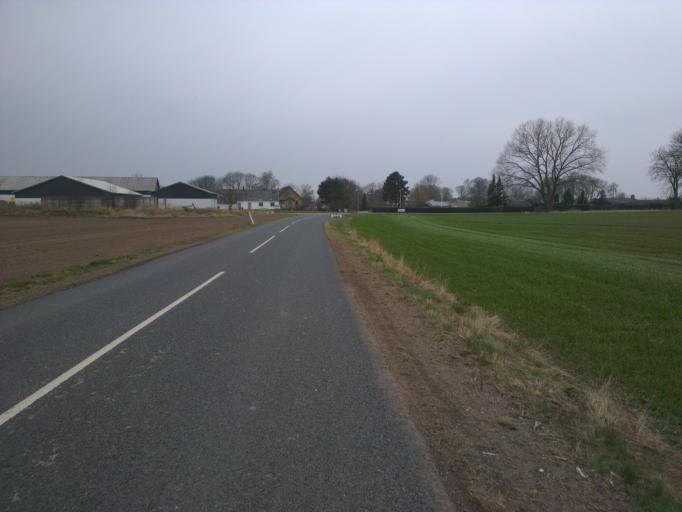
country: DK
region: Capital Region
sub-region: Frederikssund Kommune
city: Frederikssund
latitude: 55.8586
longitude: 12.1056
